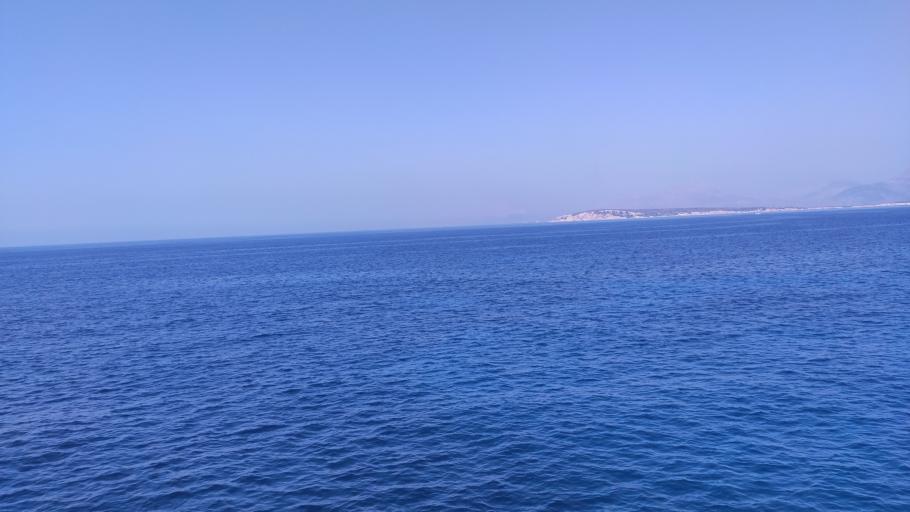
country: GR
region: South Aegean
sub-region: Nomos Dodekanisou
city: Pylion
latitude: 36.9288
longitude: 27.1305
